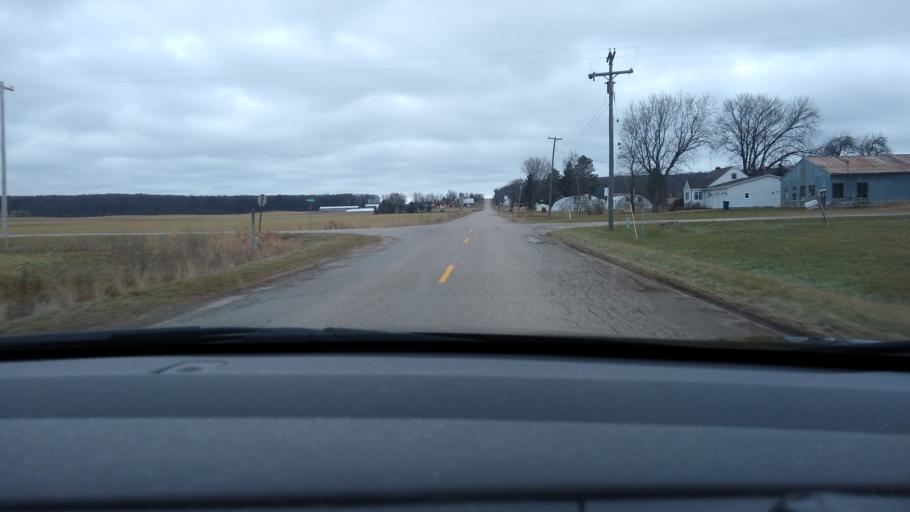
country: US
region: Michigan
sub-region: Missaukee County
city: Lake City
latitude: 44.2788
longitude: -85.0541
